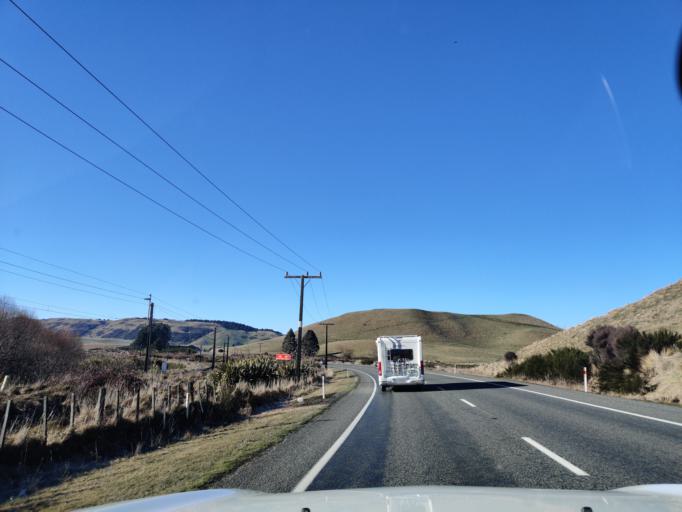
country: NZ
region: Manawatu-Wanganui
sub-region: Ruapehu District
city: Waiouru
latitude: -39.5051
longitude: 175.6744
